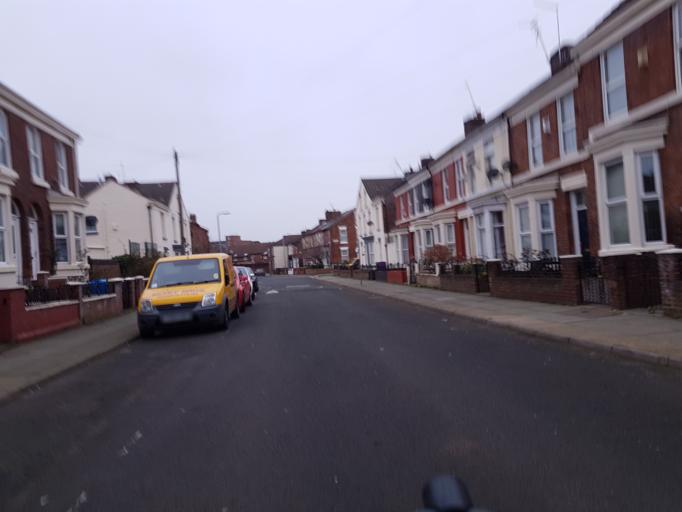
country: GB
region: England
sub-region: Liverpool
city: Liverpool
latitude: 53.4390
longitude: -2.9745
